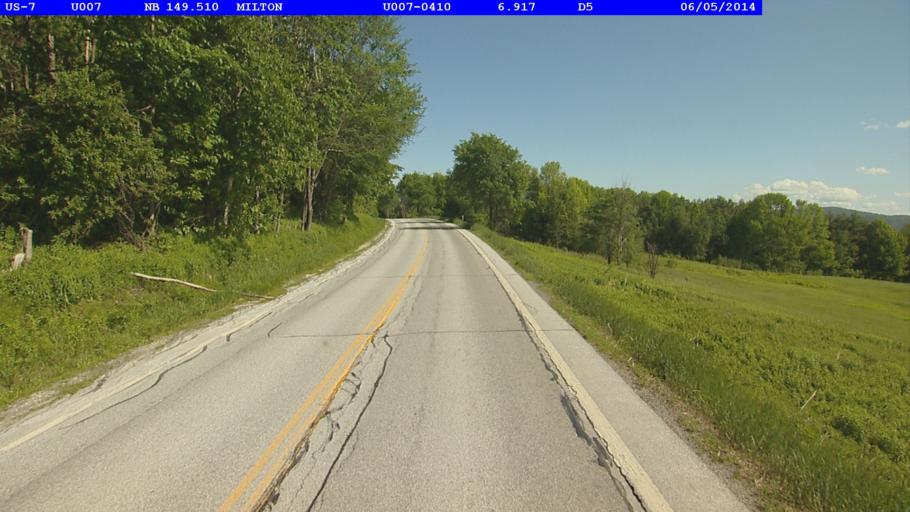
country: US
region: Vermont
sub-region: Chittenden County
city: Milton
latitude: 44.6661
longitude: -73.1113
